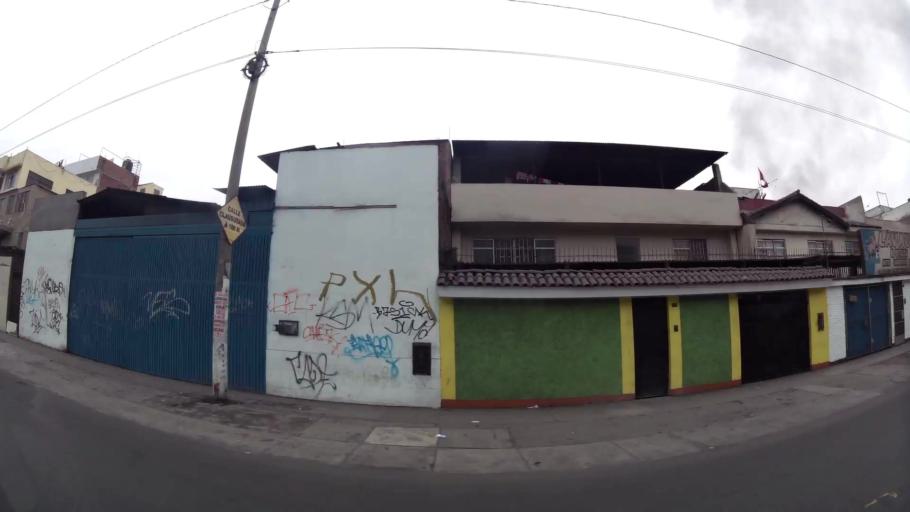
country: PE
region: Lima
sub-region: Lima
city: San Luis
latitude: -12.0821
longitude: -77.0049
